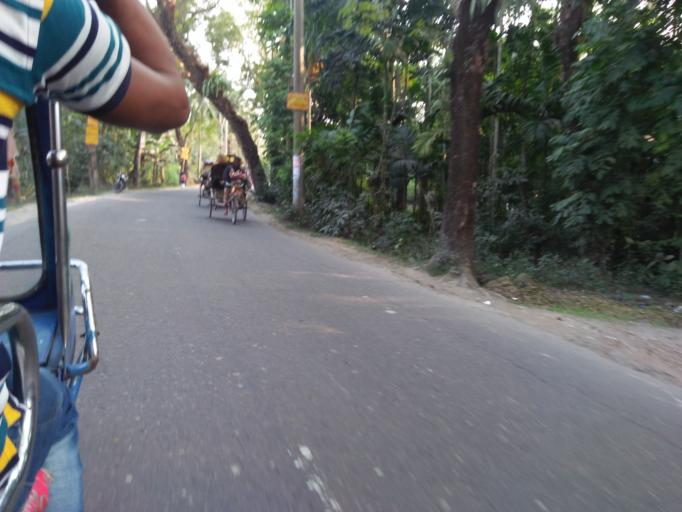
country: BD
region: Barisal
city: Bhola
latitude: 22.7005
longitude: 90.6419
